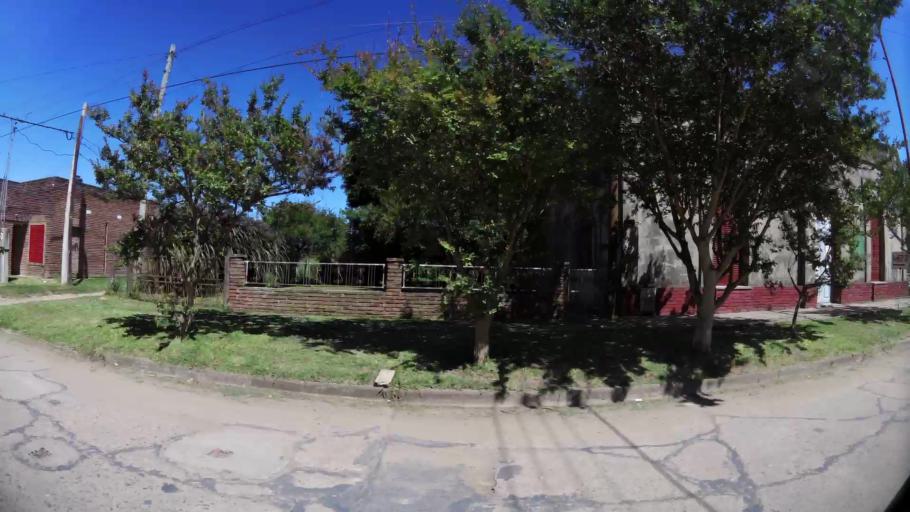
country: AR
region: Santa Fe
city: Esperanza
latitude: -31.4377
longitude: -60.9347
